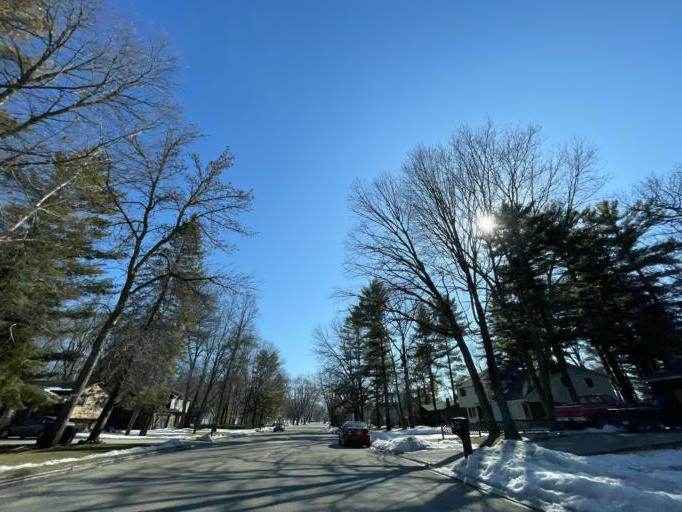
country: US
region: Wisconsin
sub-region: Brown County
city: Howard
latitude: 44.5702
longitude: -88.0804
